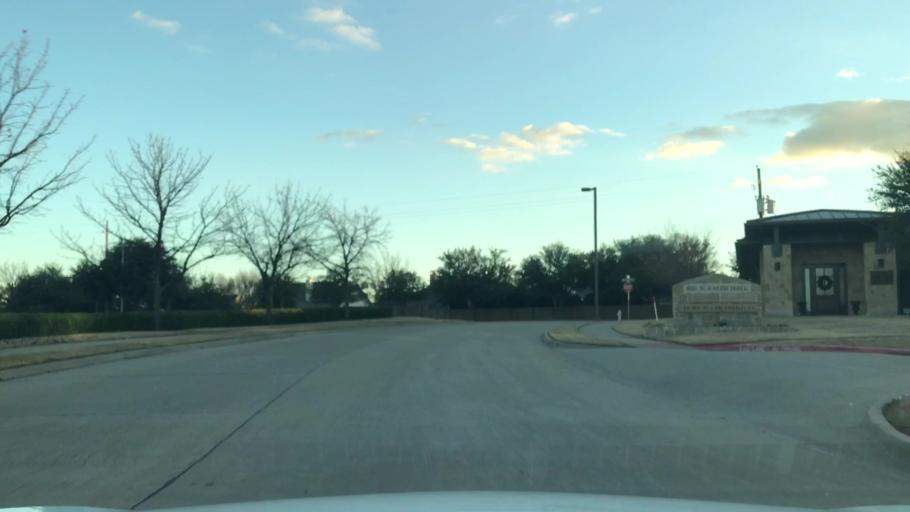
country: US
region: Texas
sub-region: Rockwall County
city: Rockwall
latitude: 32.8867
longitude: -96.4708
